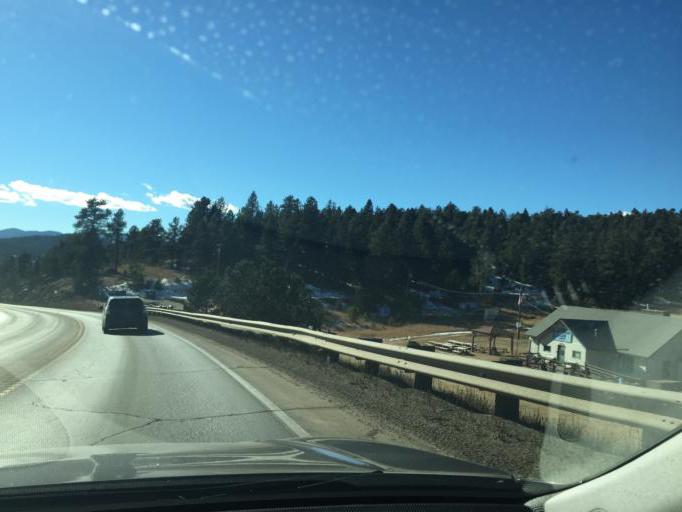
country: US
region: Colorado
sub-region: Jefferson County
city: Evergreen
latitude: 39.4878
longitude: -105.3597
